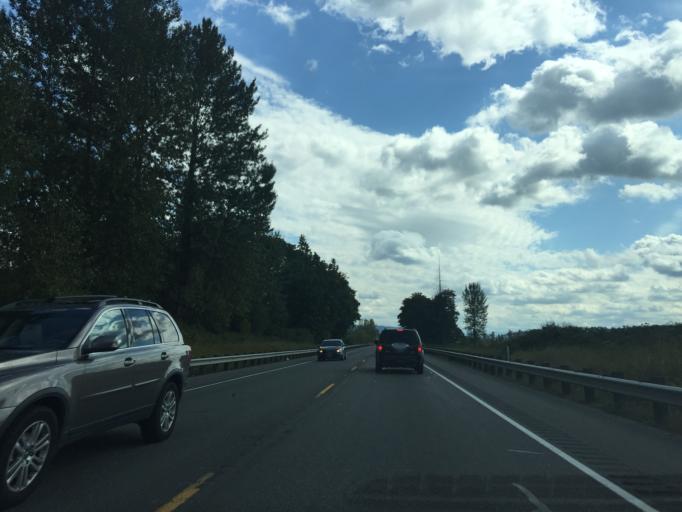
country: US
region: Washington
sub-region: Snohomish County
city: Three Lakes
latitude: 47.8935
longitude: -122.0306
